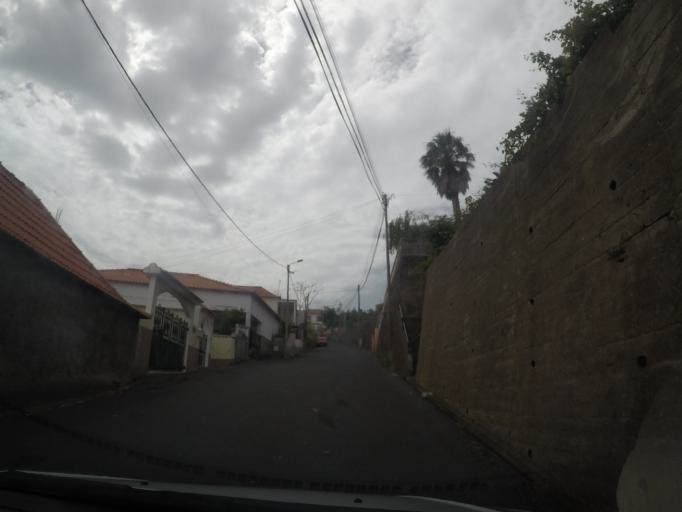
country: PT
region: Madeira
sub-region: Santa Cruz
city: Santa Cruz
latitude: 32.6888
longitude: -16.8111
